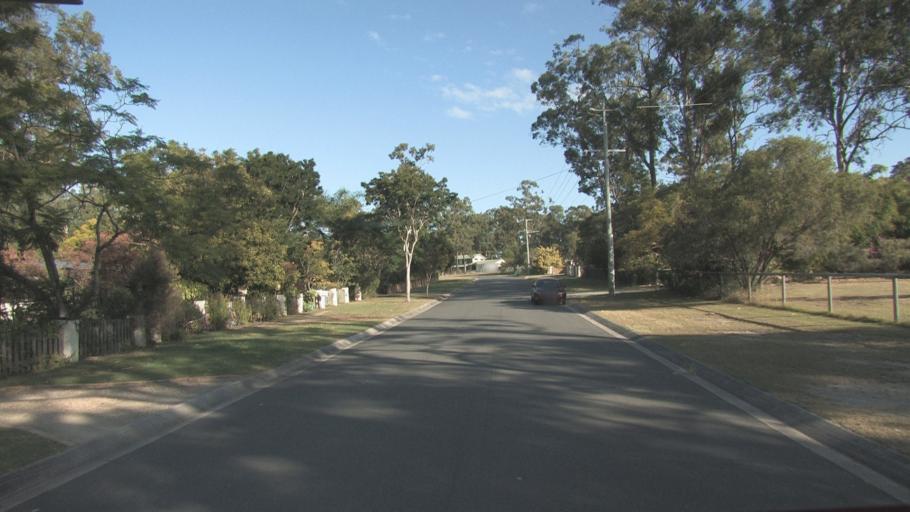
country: AU
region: Queensland
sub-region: Logan
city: Windaroo
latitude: -27.7568
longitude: 153.1917
